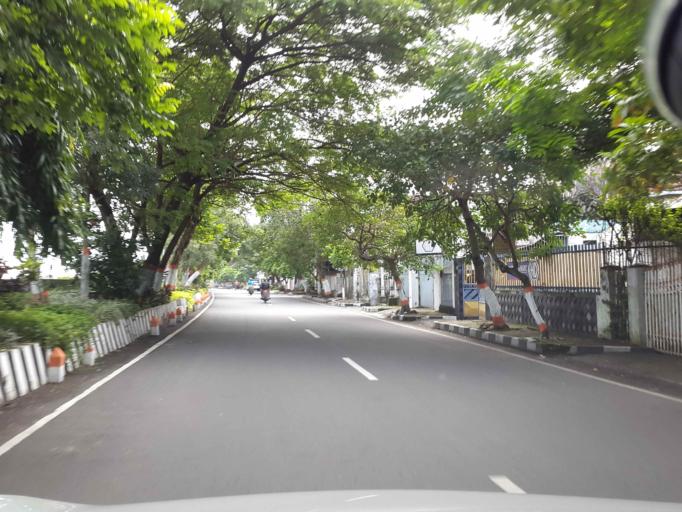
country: ID
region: East Java
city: Mojokerto
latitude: -7.4609
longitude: 112.4335
